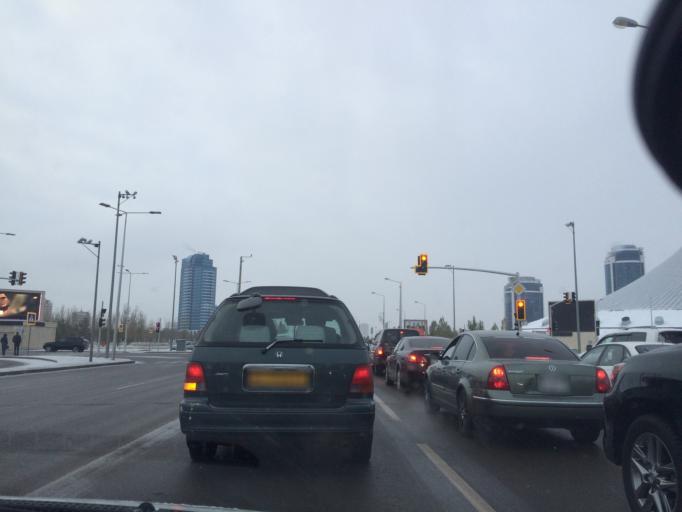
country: KZ
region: Astana Qalasy
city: Astana
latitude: 51.1349
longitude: 71.4077
